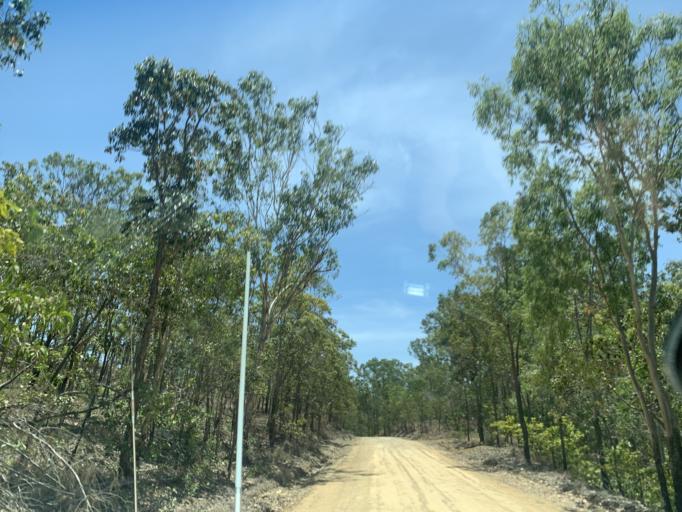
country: AU
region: Queensland
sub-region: Tablelands
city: Kuranda
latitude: -16.9194
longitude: 145.5984
